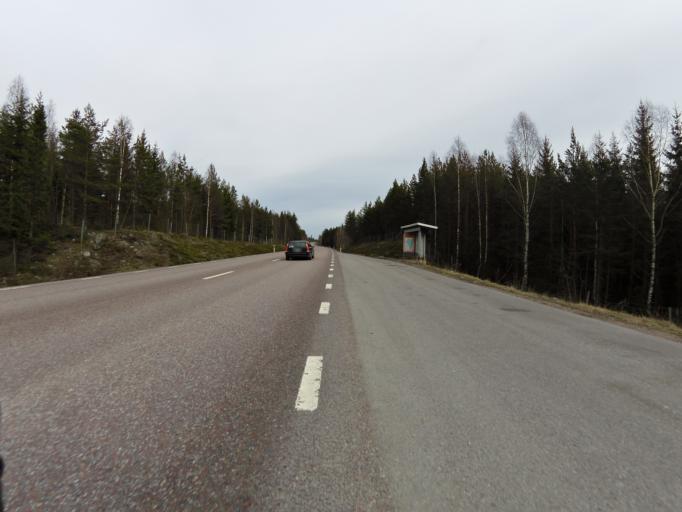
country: SE
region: Gaevleborg
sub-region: Hofors Kommun
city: Hofors
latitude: 60.5412
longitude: 16.1958
